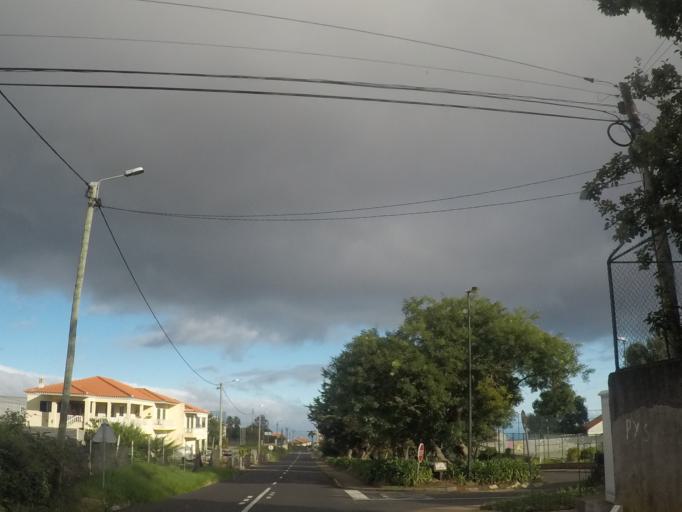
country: PT
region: Madeira
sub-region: Santa Cruz
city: Camacha
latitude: 32.6709
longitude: -16.8467
